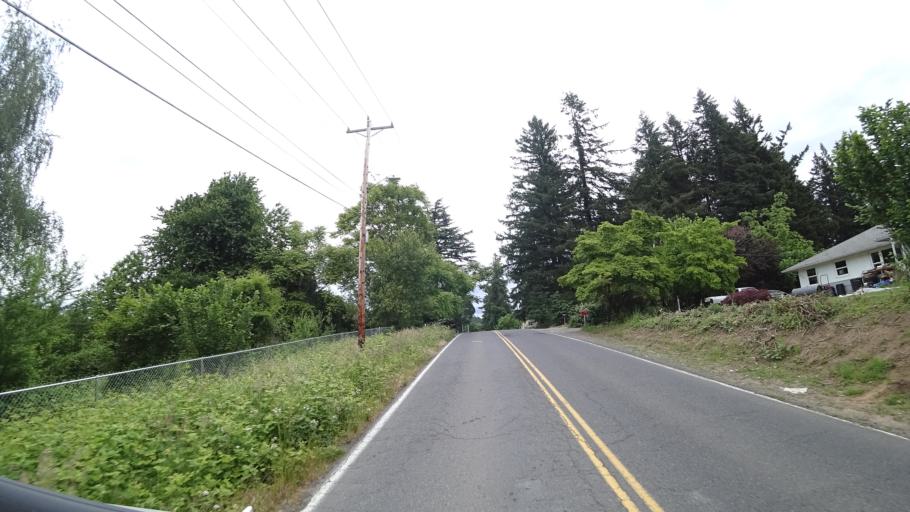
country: US
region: Oregon
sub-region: Clackamas County
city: Happy Valley
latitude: 45.4835
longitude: -122.5279
